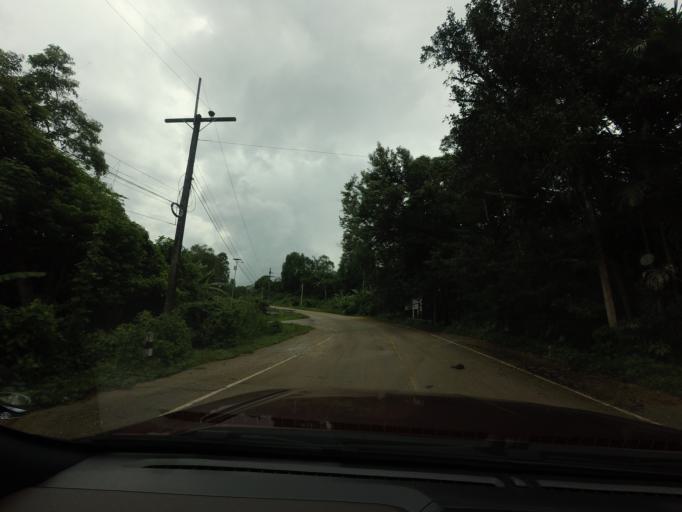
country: TH
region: Narathiwat
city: Sukhirin
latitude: 5.9863
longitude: 101.6829
